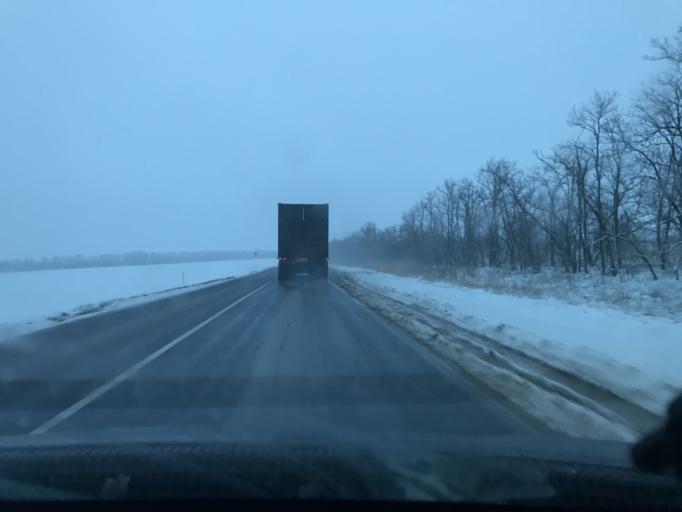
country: RU
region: Rostov
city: Letnik
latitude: 46.0732
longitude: 41.1989
